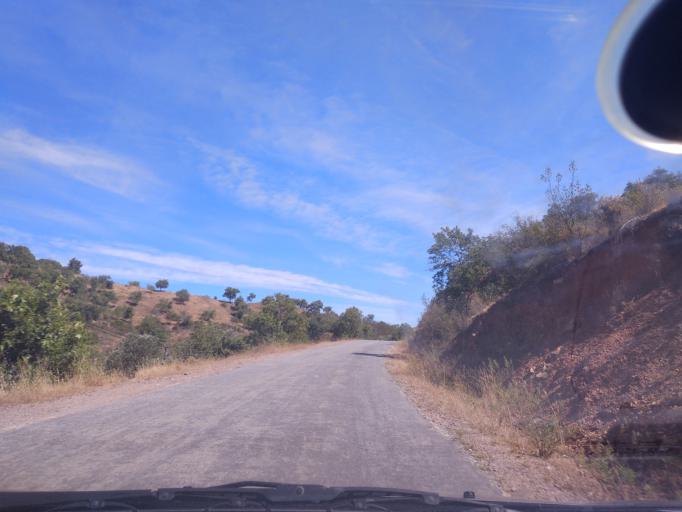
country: PT
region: Faro
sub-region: Olhao
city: Moncarapacho
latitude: 37.1573
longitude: -7.7983
